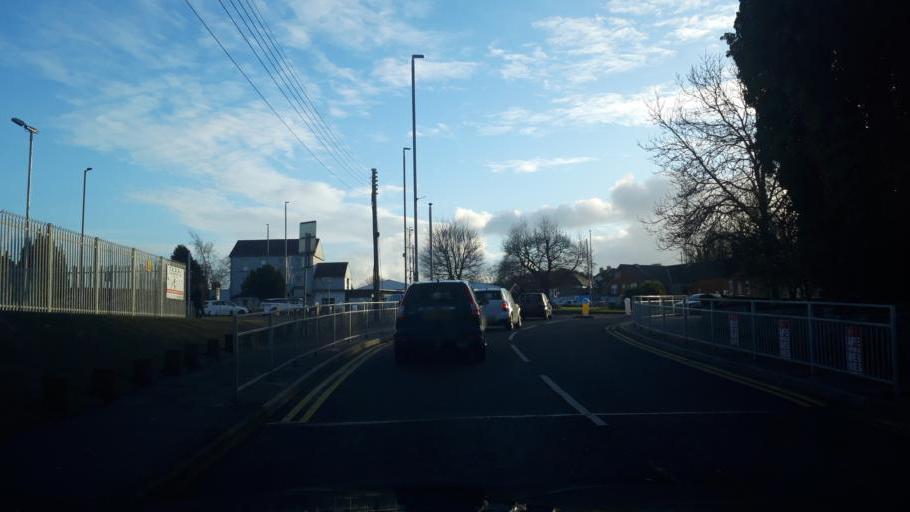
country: GB
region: Northern Ireland
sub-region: Dungannon District
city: Dungannon
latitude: 54.5093
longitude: -6.7672
